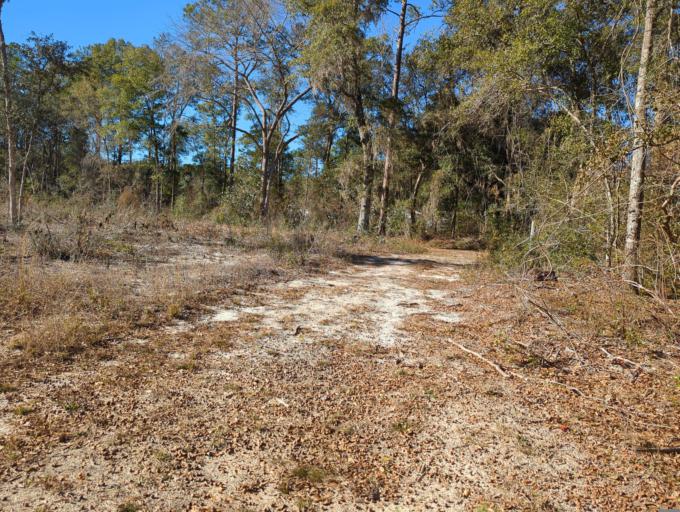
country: US
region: Florida
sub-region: Wakulla County
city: Crawfordville
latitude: 30.1864
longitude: -84.3341
